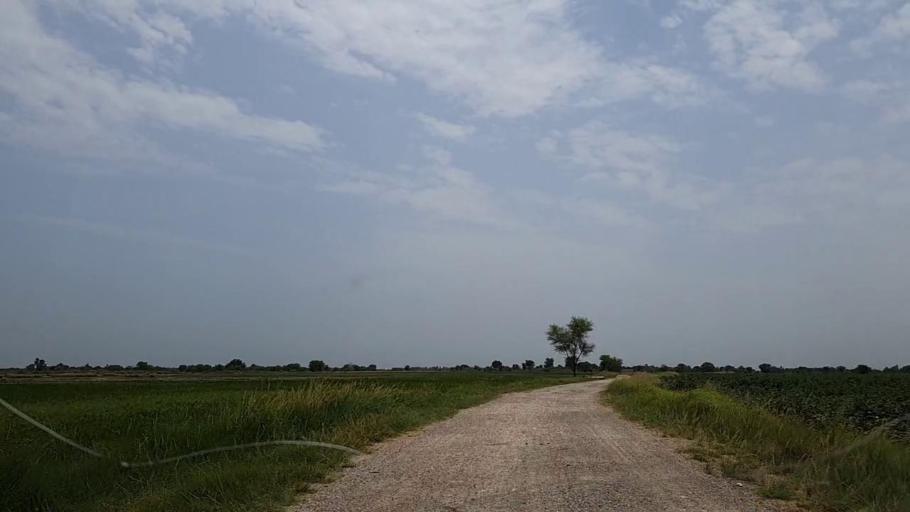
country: PK
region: Sindh
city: Tharu Shah
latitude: 26.9143
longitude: 68.0805
